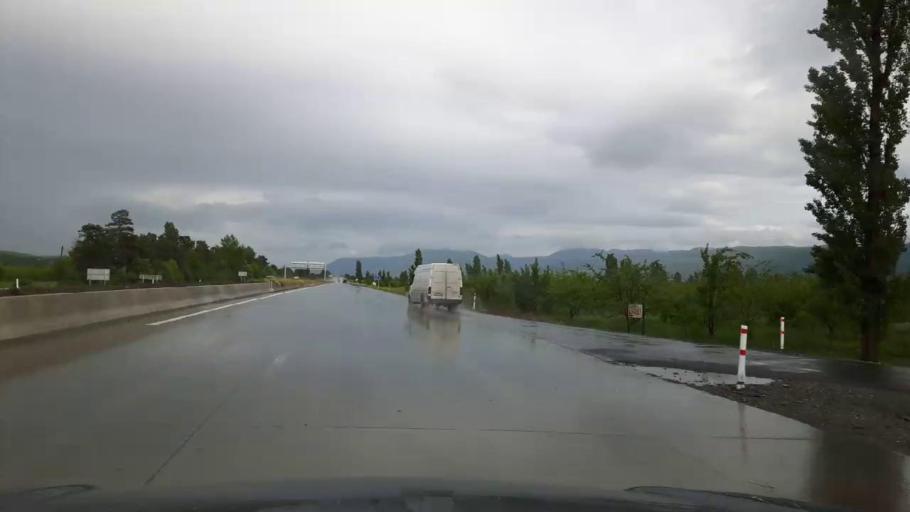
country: GE
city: Agara
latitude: 42.0473
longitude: 43.9160
